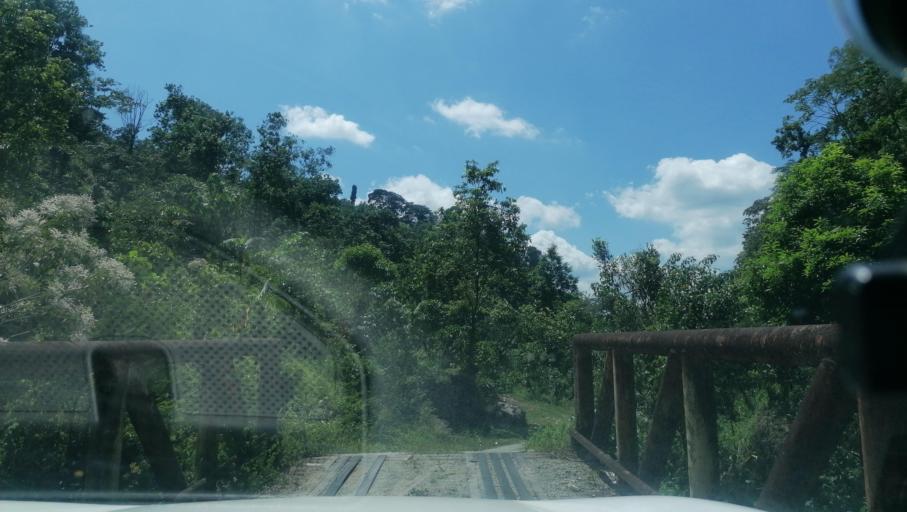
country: MX
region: Chiapas
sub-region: Union Juarez
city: Santo Domingo
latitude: 15.0715
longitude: -92.1330
